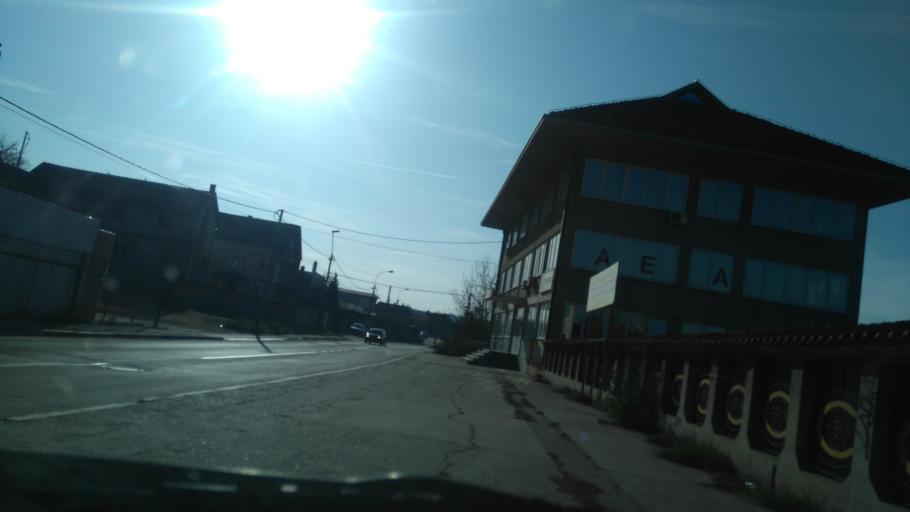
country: RS
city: Ostruznica
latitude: 44.7309
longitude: 20.3679
